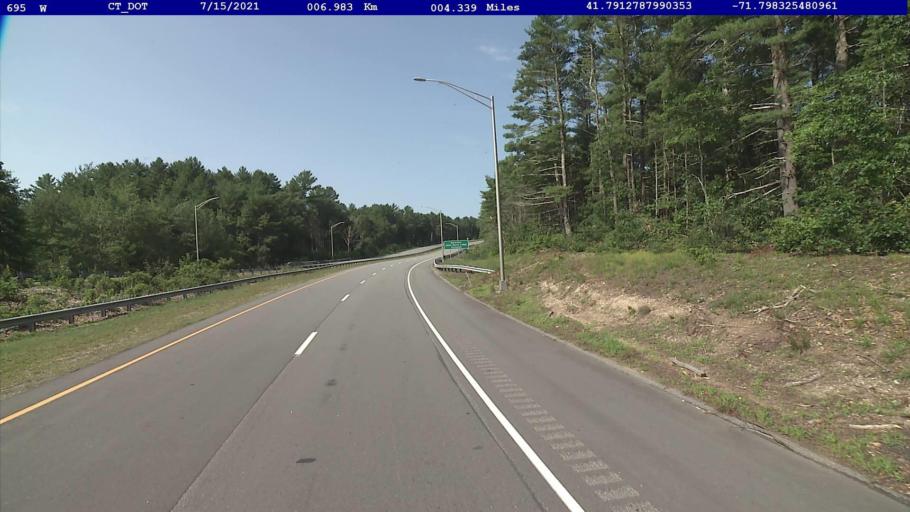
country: US
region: Rhode Island
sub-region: Providence County
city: Foster
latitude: 41.7915
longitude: -71.7985
